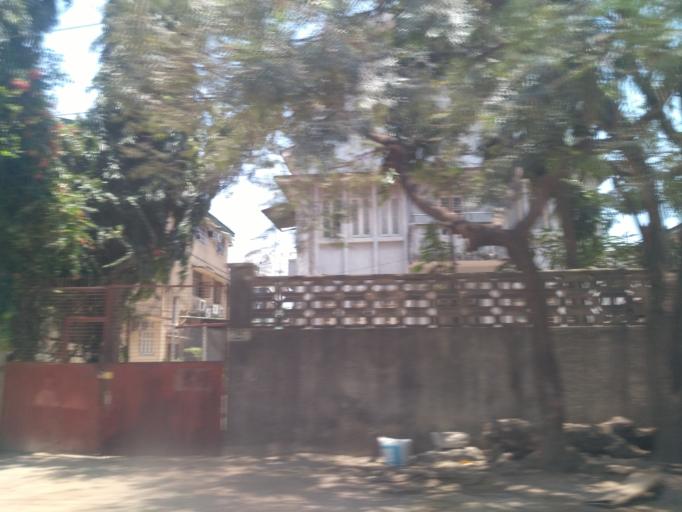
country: TZ
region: Dar es Salaam
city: Dar es Salaam
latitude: -6.8099
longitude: 39.2755
